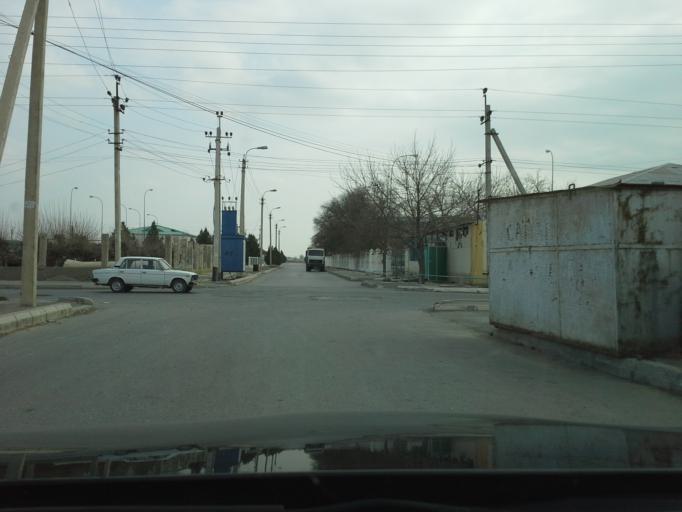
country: TM
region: Ahal
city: Abadan
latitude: 38.0373
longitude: 58.2674
